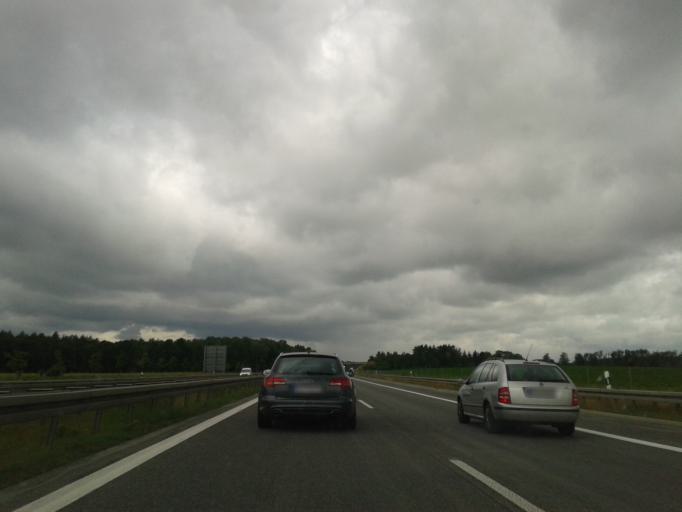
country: DE
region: Saxony
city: Naunhof
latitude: 51.2895
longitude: 12.6318
